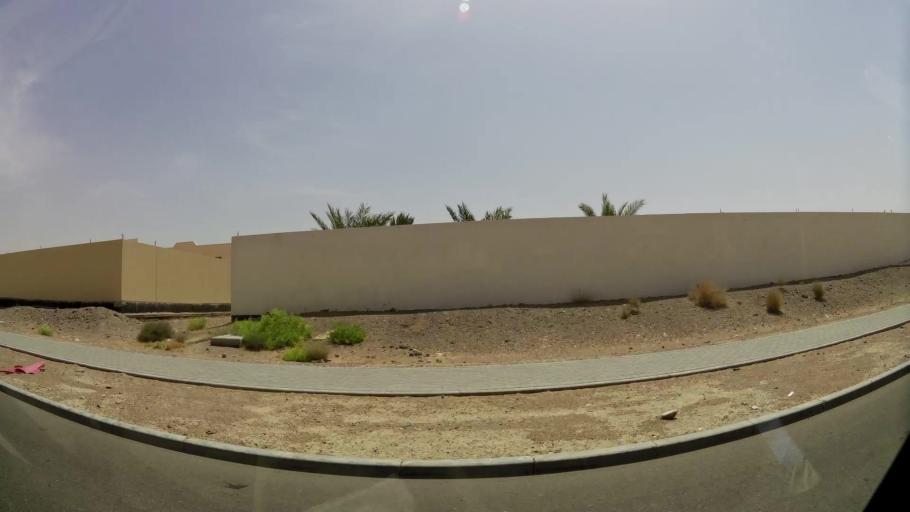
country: AE
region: Abu Dhabi
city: Al Ain
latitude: 24.1847
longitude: 55.7113
